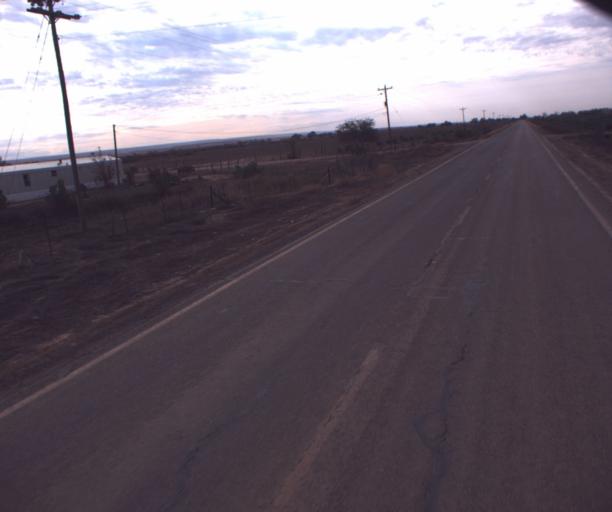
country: US
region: Arizona
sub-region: Apache County
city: Many Farms
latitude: 36.4341
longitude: -109.6069
